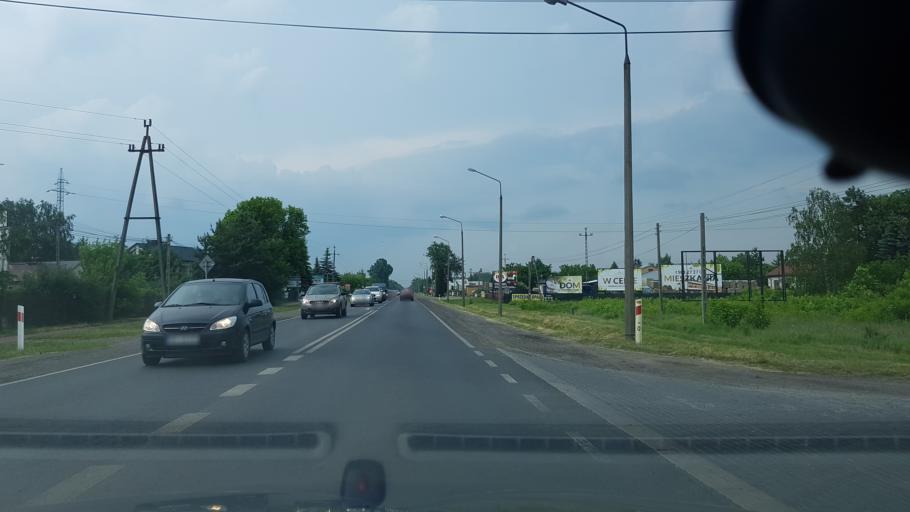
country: PL
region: Masovian Voivodeship
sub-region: Powiat legionowski
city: Michalow-Reginow
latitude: 52.4183
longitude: 20.9677
